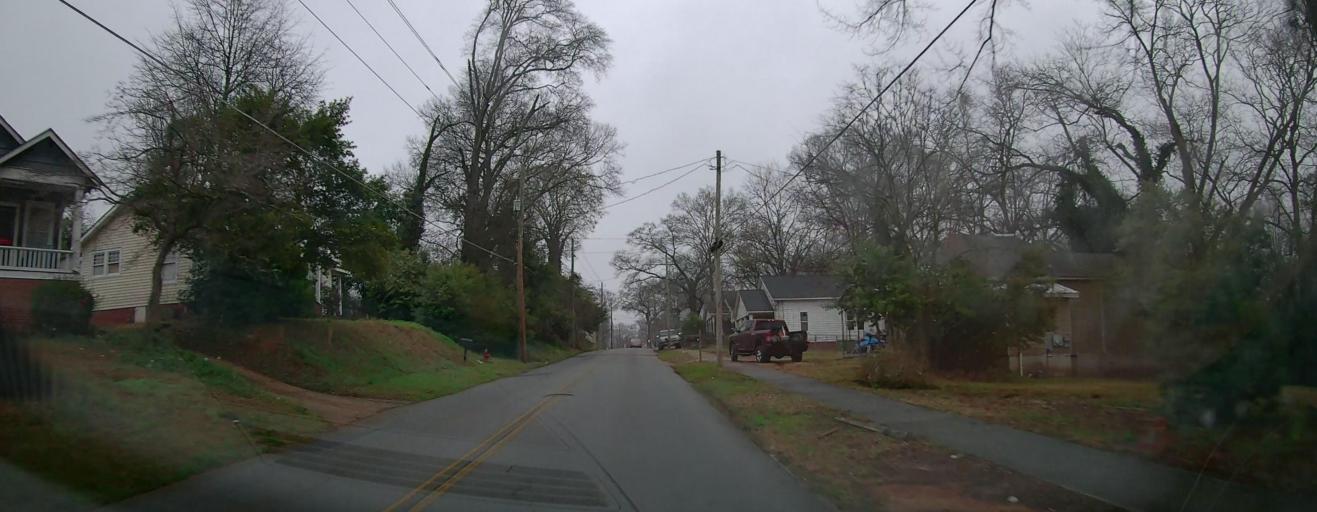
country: US
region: Georgia
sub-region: Spalding County
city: Griffin
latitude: 33.2448
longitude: -84.2707
